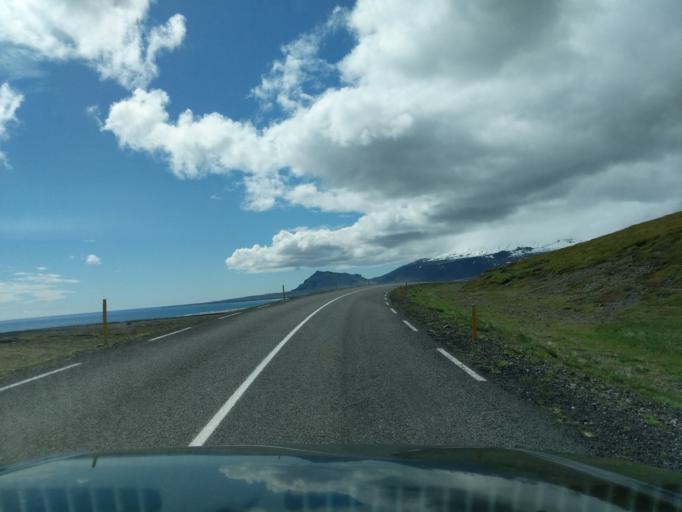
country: IS
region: West
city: Olafsvik
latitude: 64.8244
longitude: -23.4394
